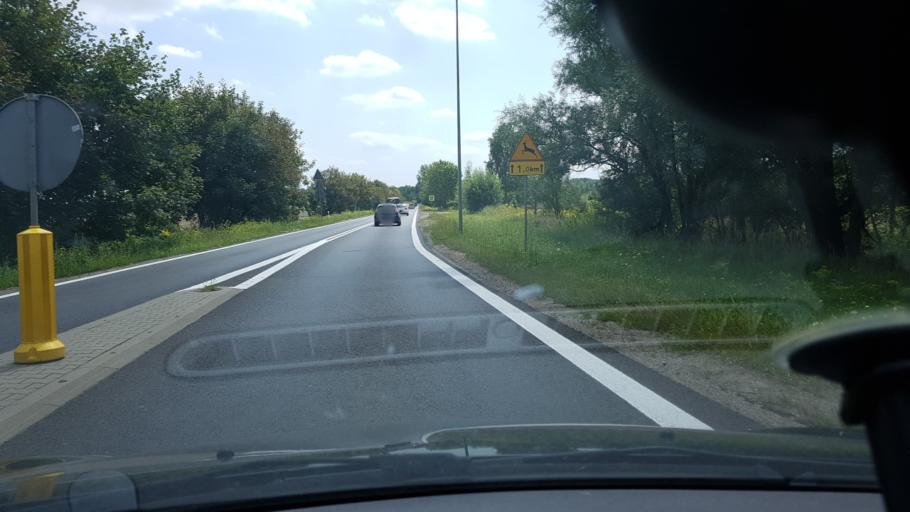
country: PL
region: Silesian Voivodeship
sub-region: Powiat bierunsko-ledzinski
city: Bierun
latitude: 50.0910
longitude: 19.1057
